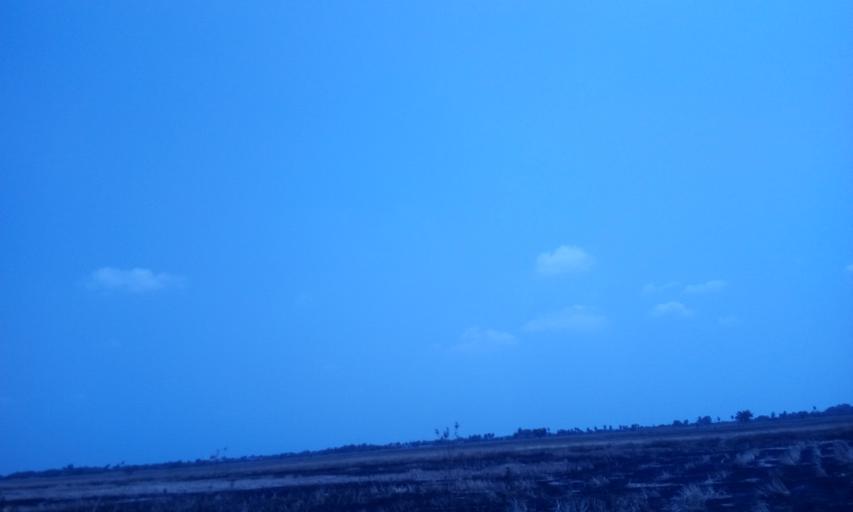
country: TH
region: Chachoengsao
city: Bang Nam Priao
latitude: 13.9569
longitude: 100.9705
